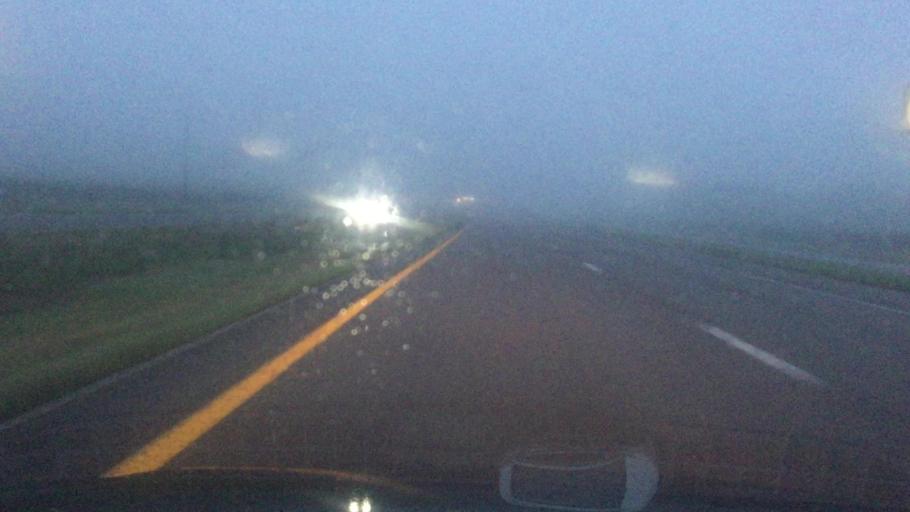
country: US
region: Missouri
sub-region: Montgomery County
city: Montgomery City
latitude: 38.8854
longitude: -91.4061
